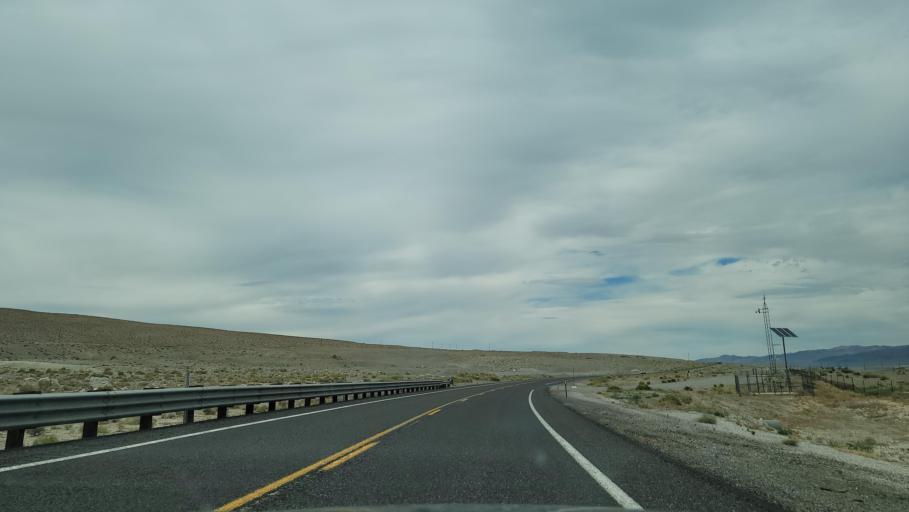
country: US
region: Nevada
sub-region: Mineral County
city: Hawthorne
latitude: 38.5861
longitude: -118.7090
